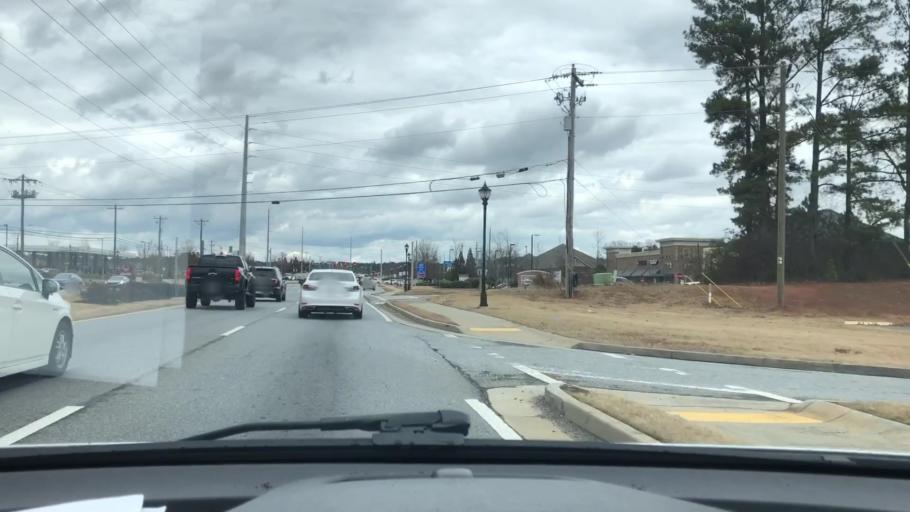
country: US
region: Georgia
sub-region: Forsyth County
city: Cumming
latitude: 34.1489
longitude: -84.1732
